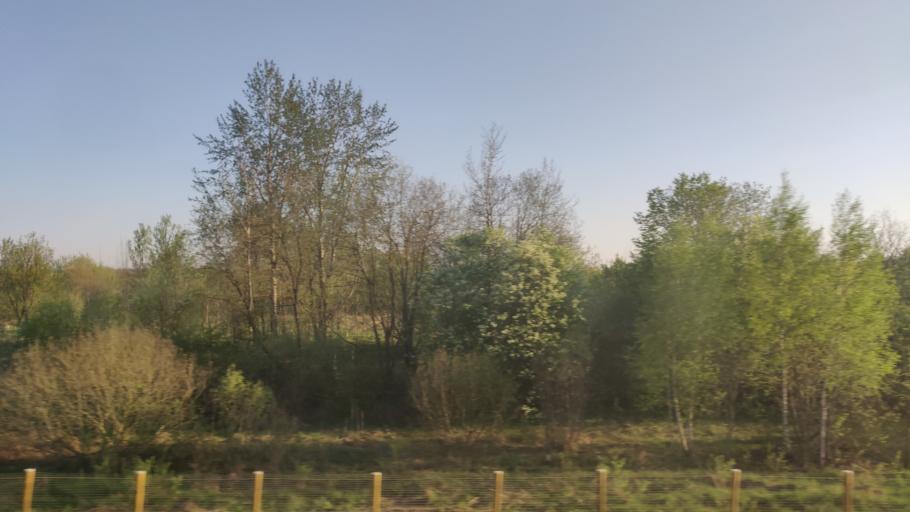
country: LT
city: Baltoji Voke
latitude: 54.6325
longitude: 25.1354
